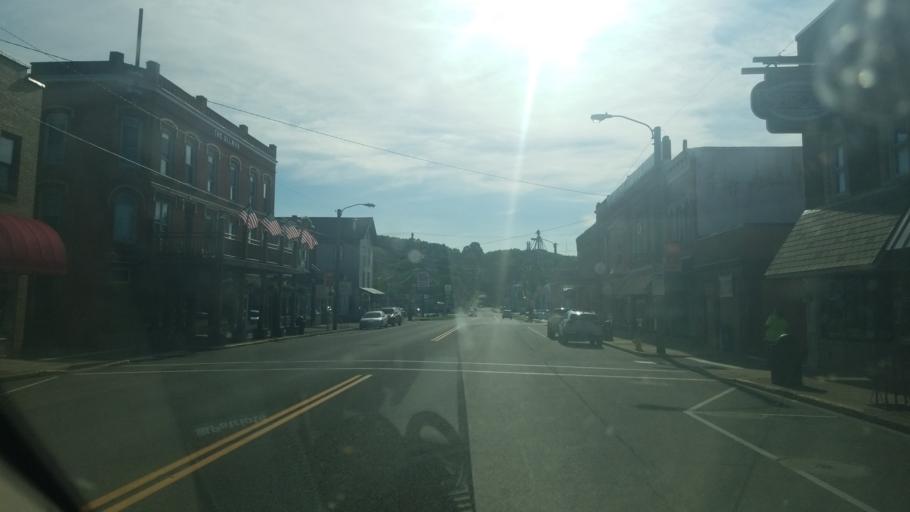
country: US
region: Ohio
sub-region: Ashland County
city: Loudonville
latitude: 40.6348
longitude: -82.2355
